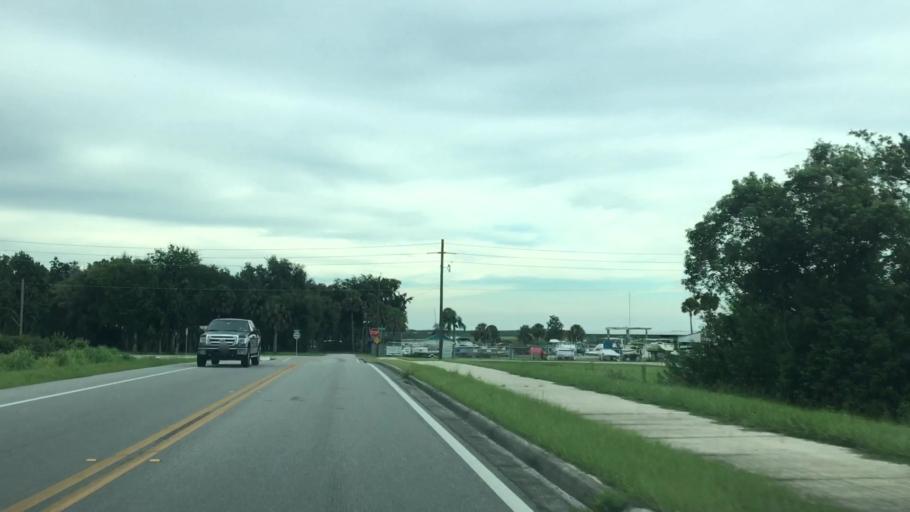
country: US
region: Florida
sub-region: Seminole County
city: Midway
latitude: 28.8006
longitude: -81.2143
